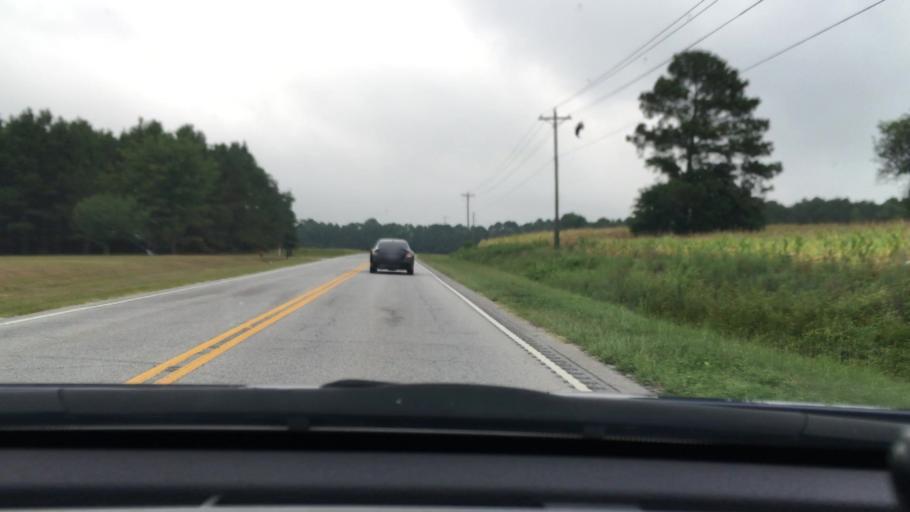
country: US
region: South Carolina
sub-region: Florence County
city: Timmonsville
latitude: 34.1955
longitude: -80.0398
